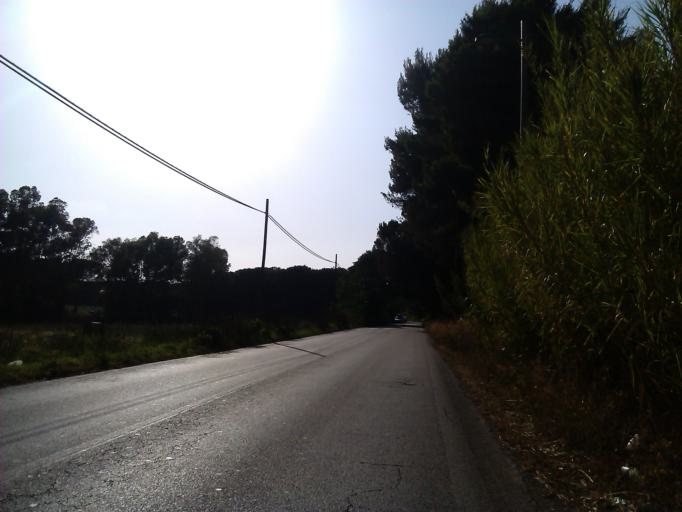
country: IT
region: Latium
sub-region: Citta metropolitana di Roma Capitale
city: Rome
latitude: 41.8260
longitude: 12.5258
